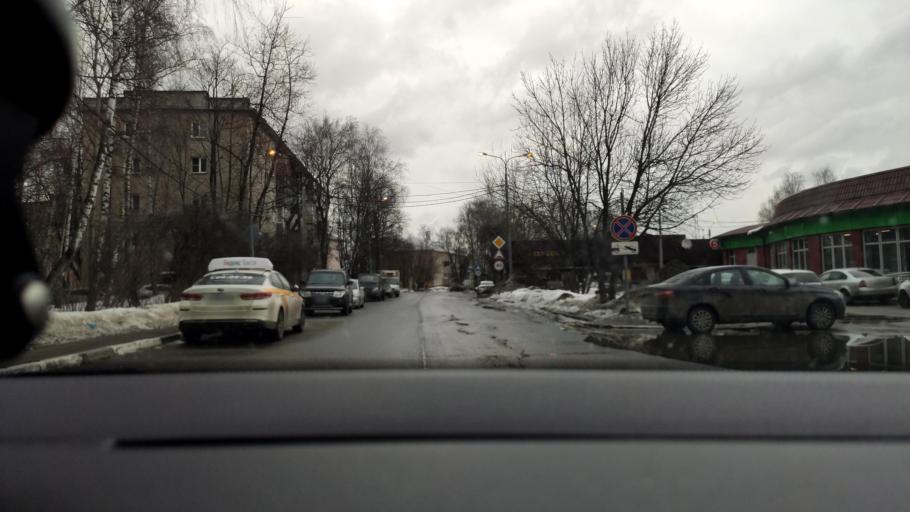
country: RU
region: Moskovskaya
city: Druzhba
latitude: 55.8839
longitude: 37.7550
